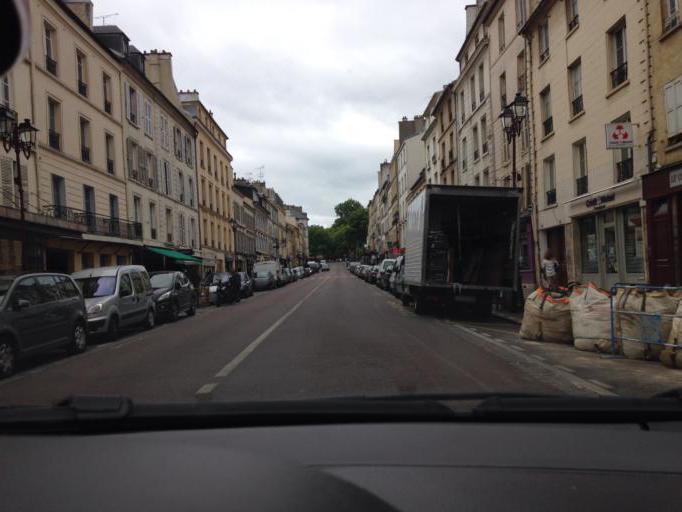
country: FR
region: Ile-de-France
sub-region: Departement des Yvelines
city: Versailles
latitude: 48.8063
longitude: 2.1331
